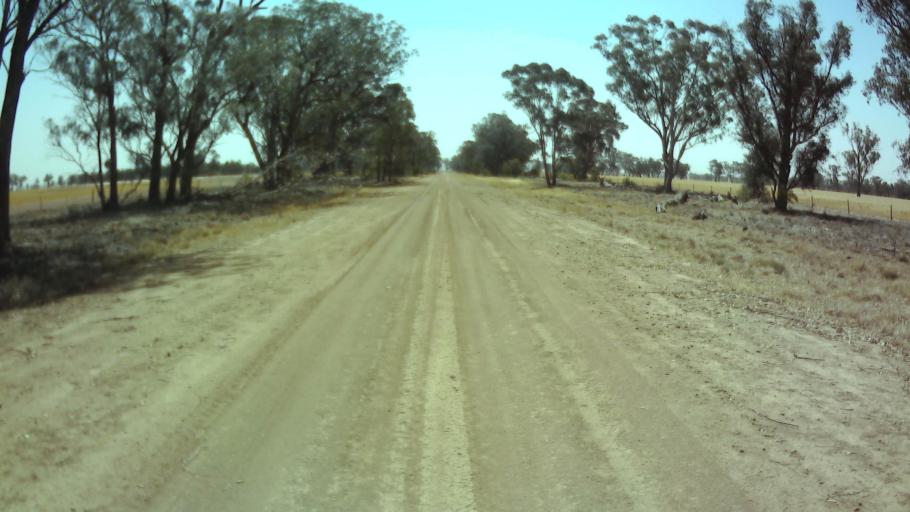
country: AU
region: New South Wales
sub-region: Weddin
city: Grenfell
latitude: -33.9431
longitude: 147.8135
